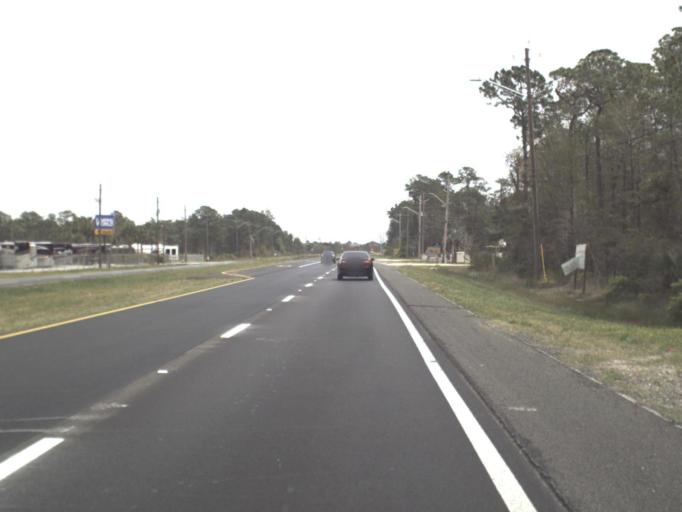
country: US
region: Florida
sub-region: Santa Rosa County
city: Woodlawn Beach
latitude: 30.4038
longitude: -86.9647
